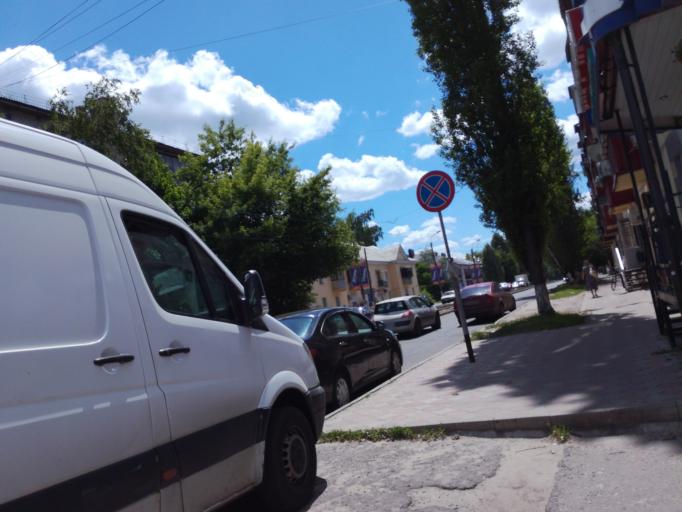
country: RU
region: Kursk
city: Kursk
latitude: 51.7465
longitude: 36.2468
